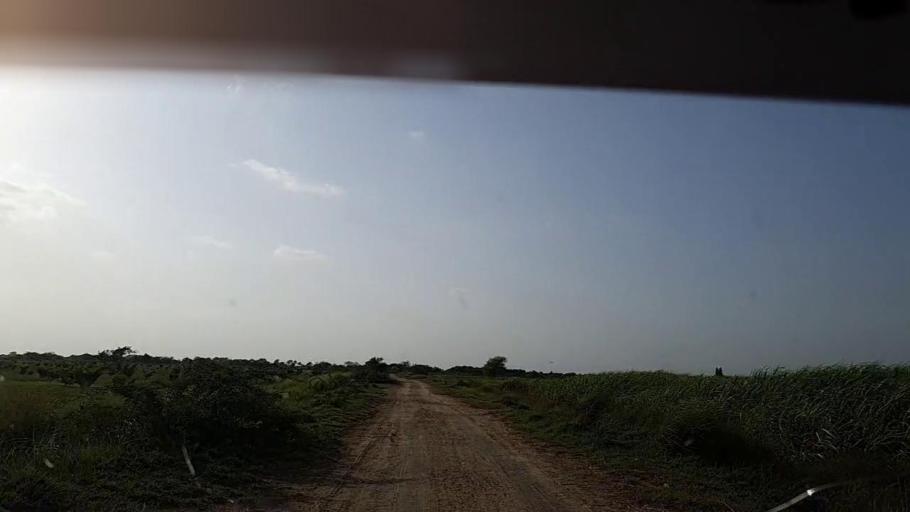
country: PK
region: Sindh
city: Badin
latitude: 24.5666
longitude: 68.8825
